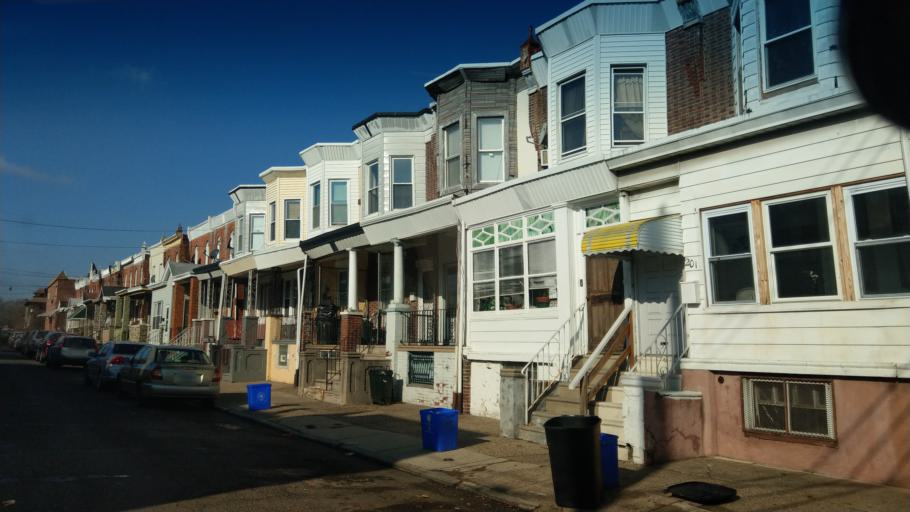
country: US
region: Pennsylvania
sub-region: Montgomery County
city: Rockledge
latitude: 40.0237
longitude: -75.1280
